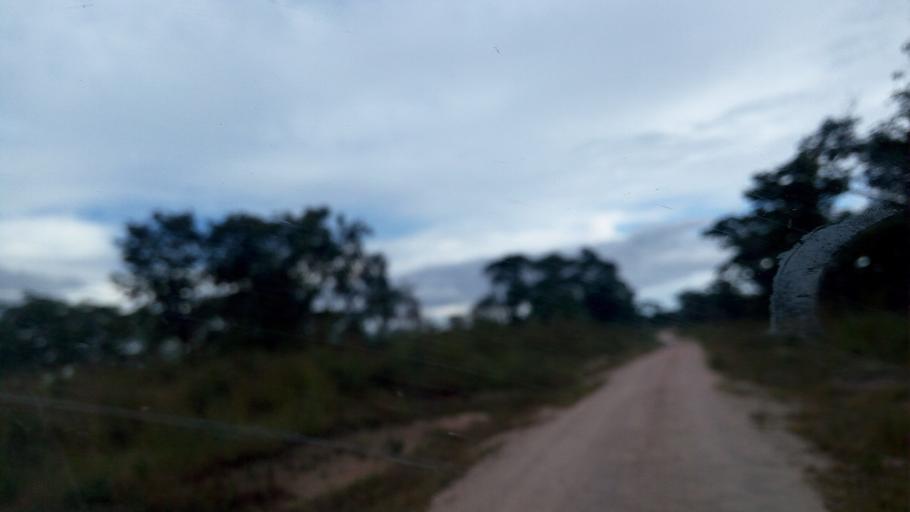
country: CD
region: Katanga
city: Kalemie
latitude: -6.6011
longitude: 29.0417
